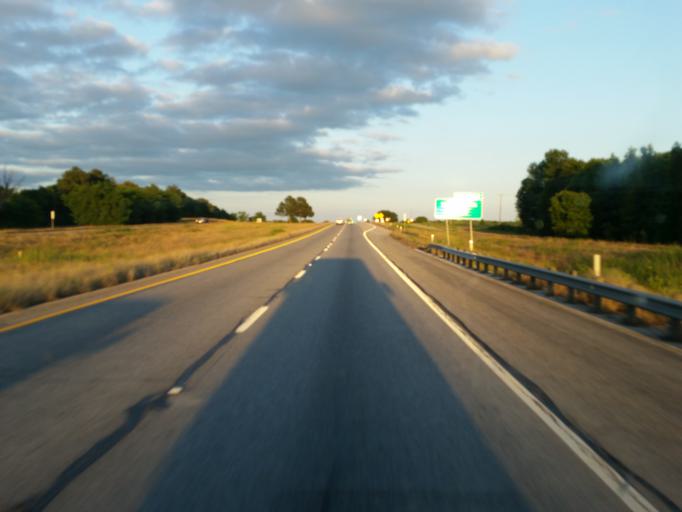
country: US
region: Texas
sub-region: Van Zandt County
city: Van
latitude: 32.5297
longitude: -95.7223
